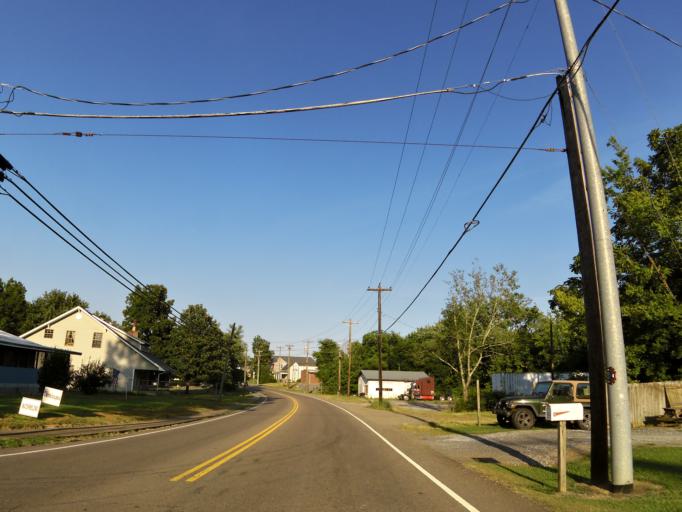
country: US
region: Tennessee
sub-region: McMinn County
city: Englewood
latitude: 35.4267
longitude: -84.4917
